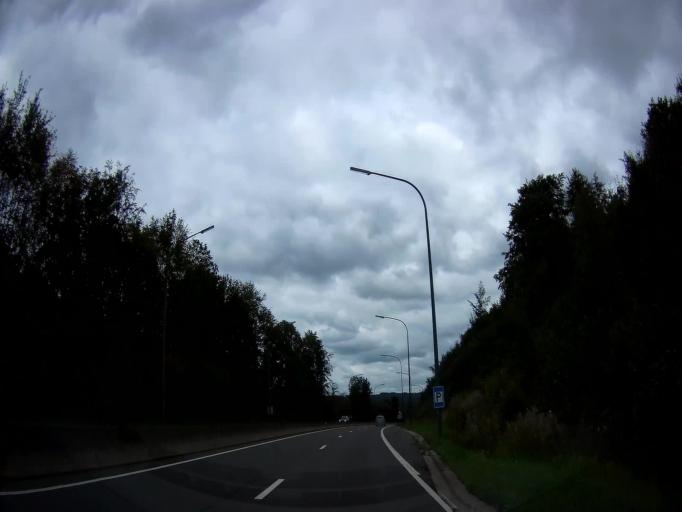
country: BE
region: Wallonia
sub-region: Province du Luxembourg
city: Marche-en-Famenne
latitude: 50.2119
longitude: 5.3634
